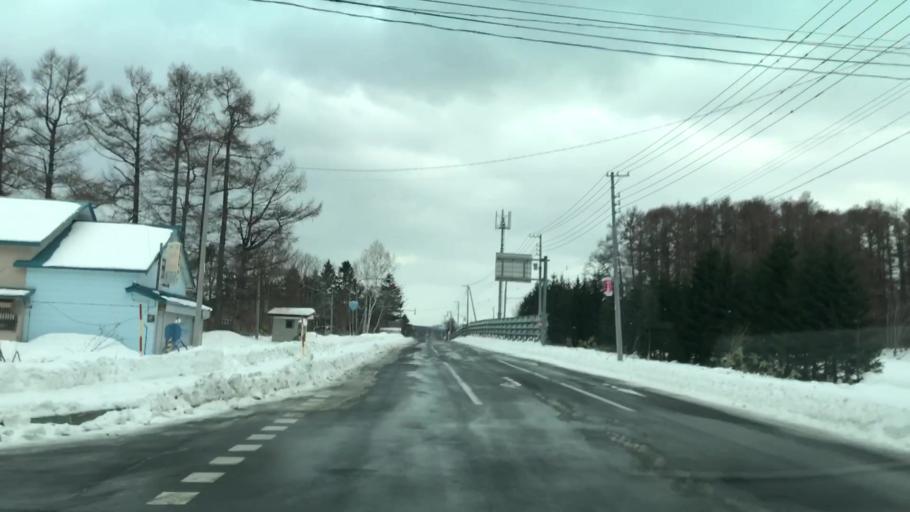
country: JP
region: Hokkaido
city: Yoichi
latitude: 43.3134
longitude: 140.5443
